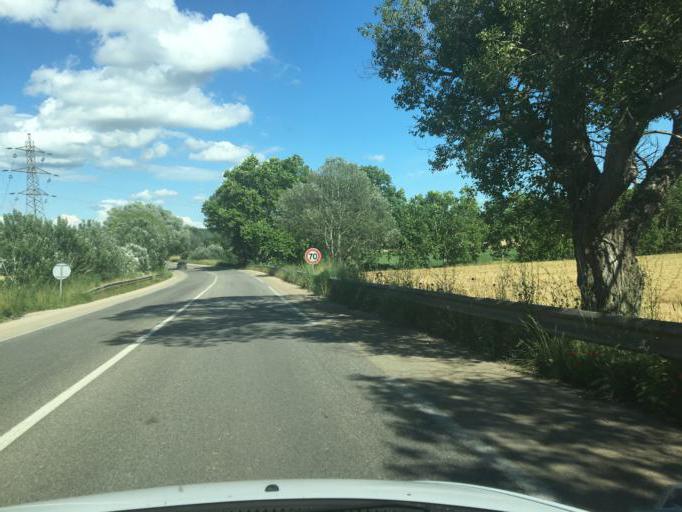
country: FR
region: Provence-Alpes-Cote d'Azur
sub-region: Departement des Bouches-du-Rhone
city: Eguilles
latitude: 43.5438
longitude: 5.3527
